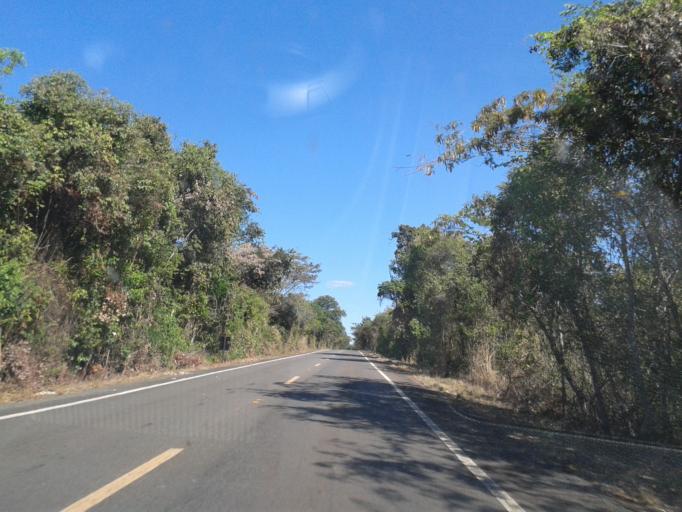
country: BR
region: Goias
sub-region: Sao Miguel Do Araguaia
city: Sao Miguel do Araguaia
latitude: -13.8042
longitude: -50.3423
